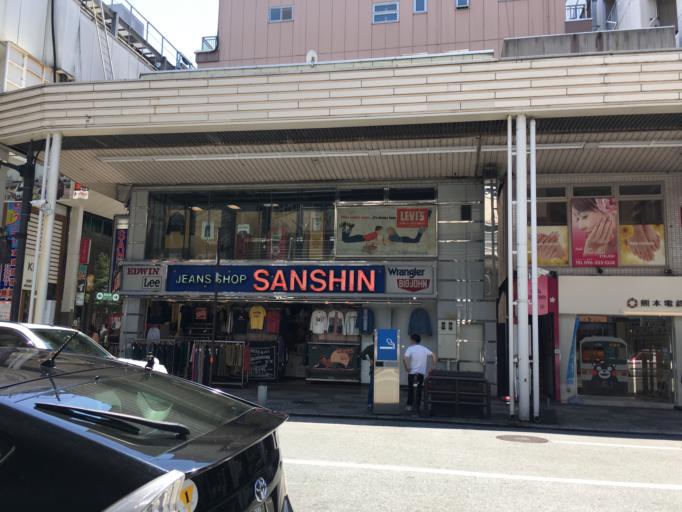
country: JP
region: Kumamoto
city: Kumamoto
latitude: 32.8006
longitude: 130.7080
